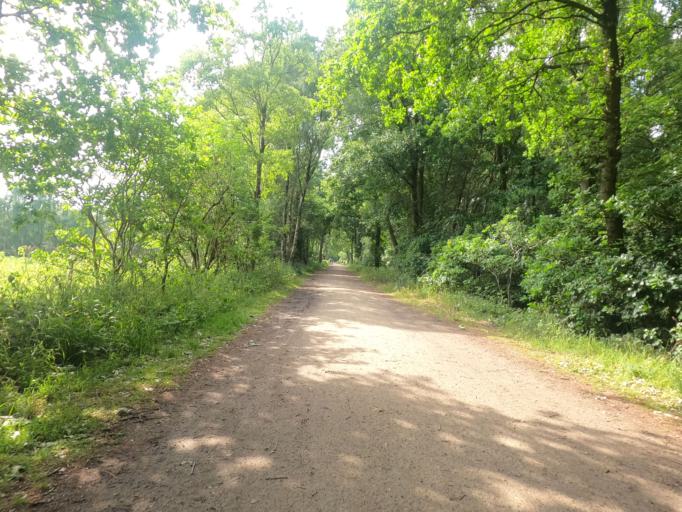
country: GB
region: England
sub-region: Cheshire West and Chester
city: Cuddington
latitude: 53.2131
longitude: -2.5951
